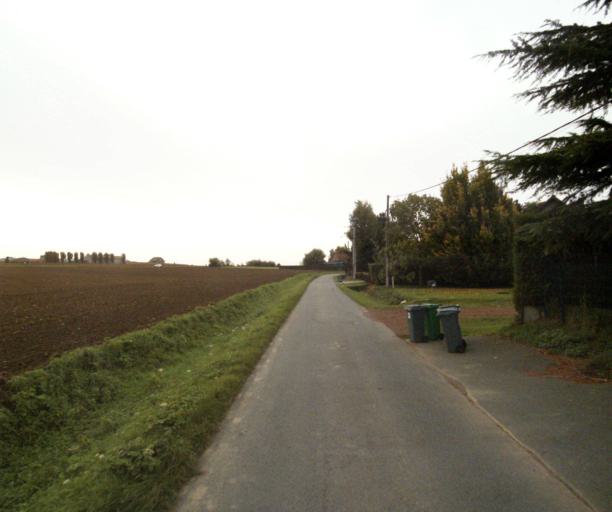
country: FR
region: Nord-Pas-de-Calais
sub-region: Departement du Nord
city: Aubers
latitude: 50.5867
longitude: 2.8166
